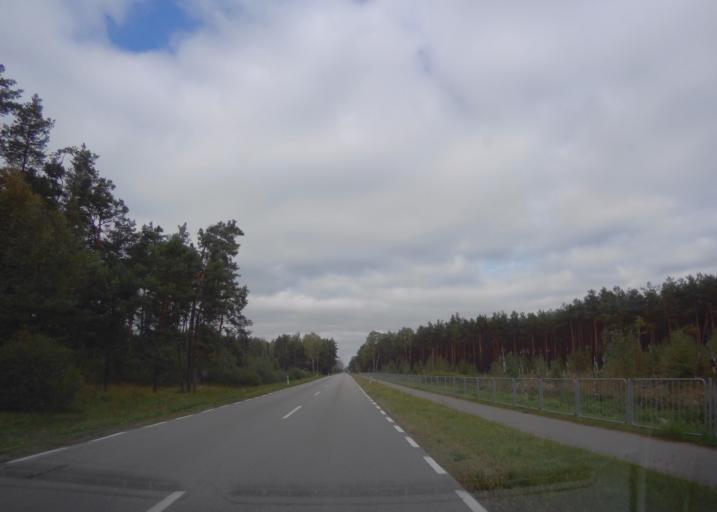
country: PL
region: Lublin Voivodeship
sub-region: Powiat wlodawski
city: Wlodawa
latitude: 51.4848
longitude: 23.5164
